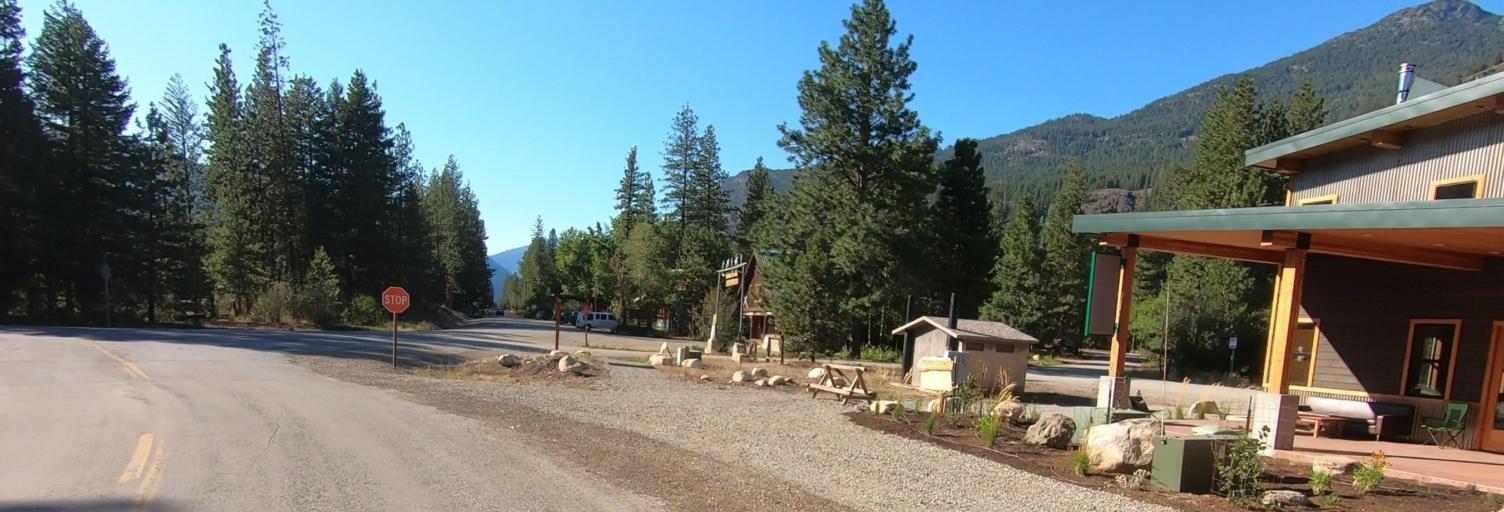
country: US
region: Washington
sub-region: Chelan County
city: Granite Falls
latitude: 48.5923
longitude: -120.4043
